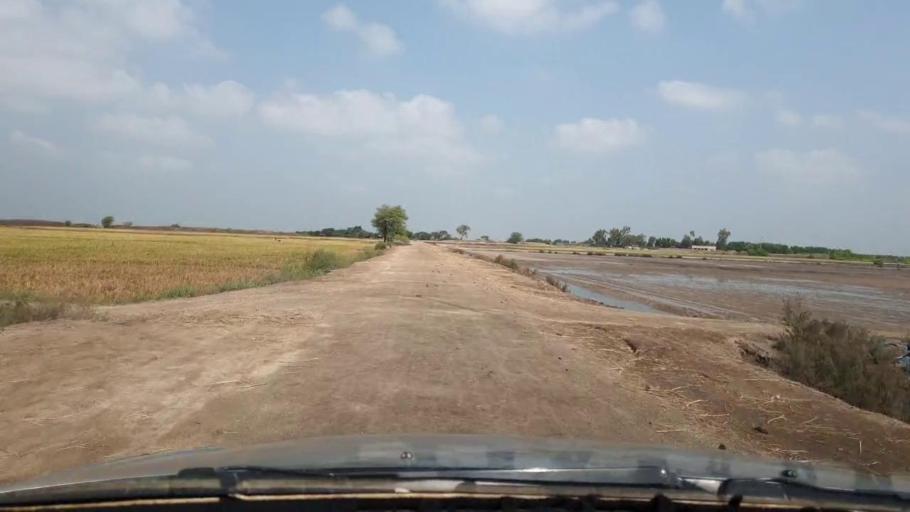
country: PK
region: Sindh
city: Matli
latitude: 25.0907
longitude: 68.6915
